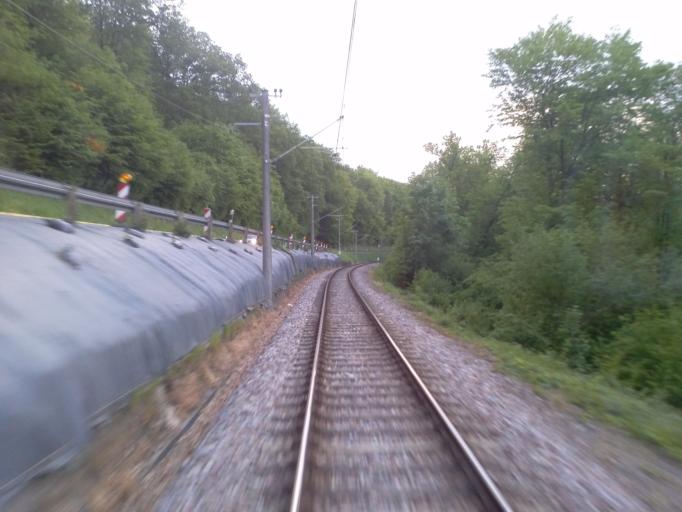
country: DE
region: Baden-Wuerttemberg
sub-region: Karlsruhe Region
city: Ettlingen
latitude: 48.9039
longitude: 8.4543
